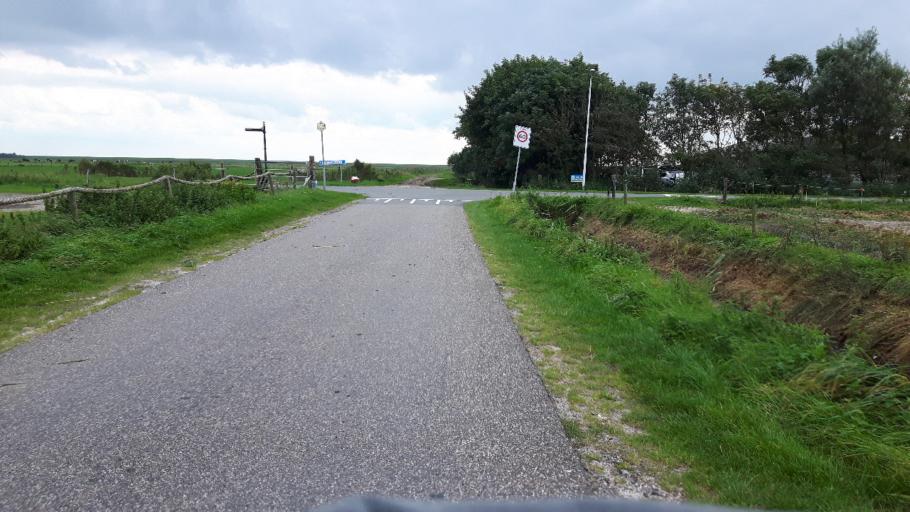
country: NL
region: Friesland
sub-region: Gemeente Ameland
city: Nes
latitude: 53.4501
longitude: 5.8185
